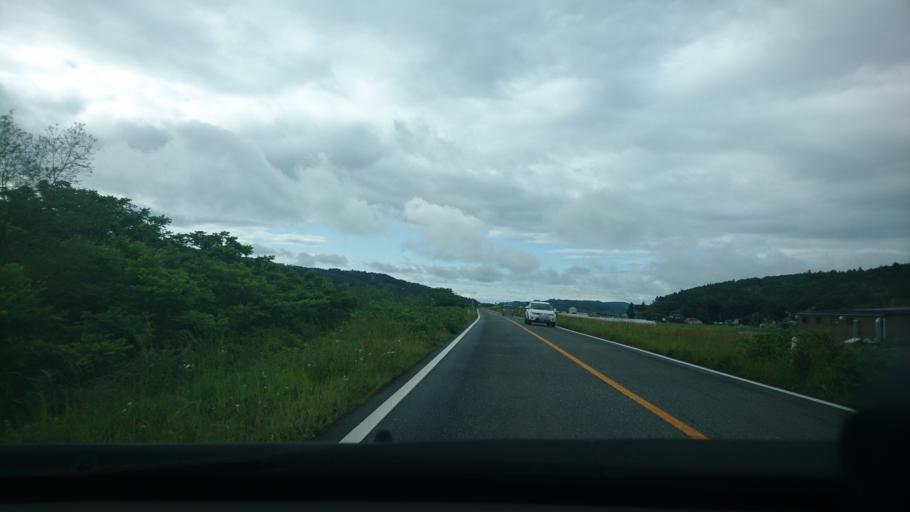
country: JP
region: Miyagi
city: Wakuya
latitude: 38.6294
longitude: 141.2923
